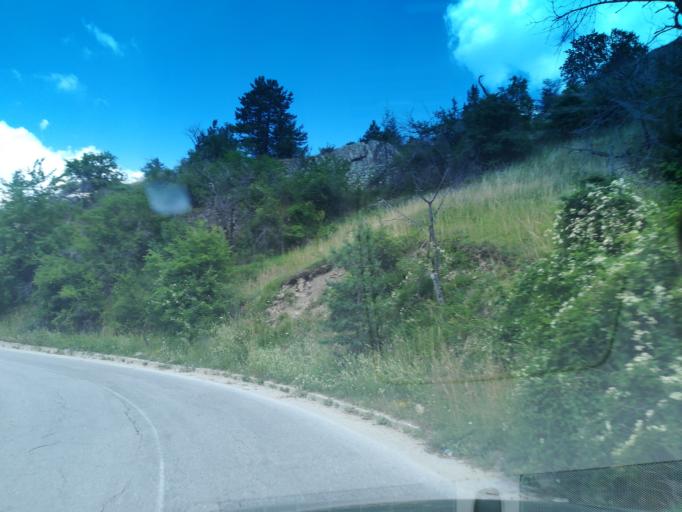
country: BG
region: Smolyan
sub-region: Obshtina Chepelare
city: Chepelare
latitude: 41.6663
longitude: 24.7756
